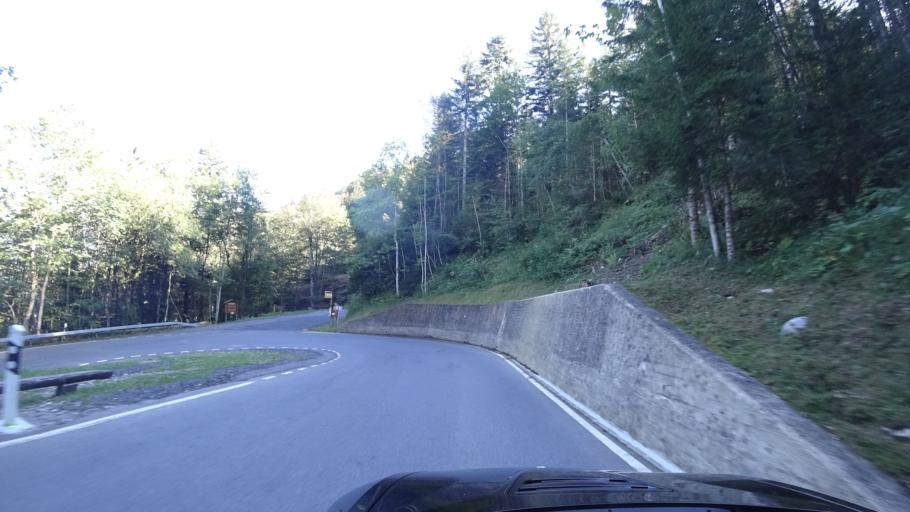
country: CH
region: Obwalden
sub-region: Obwalden
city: Giswil
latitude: 46.8286
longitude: 8.1319
